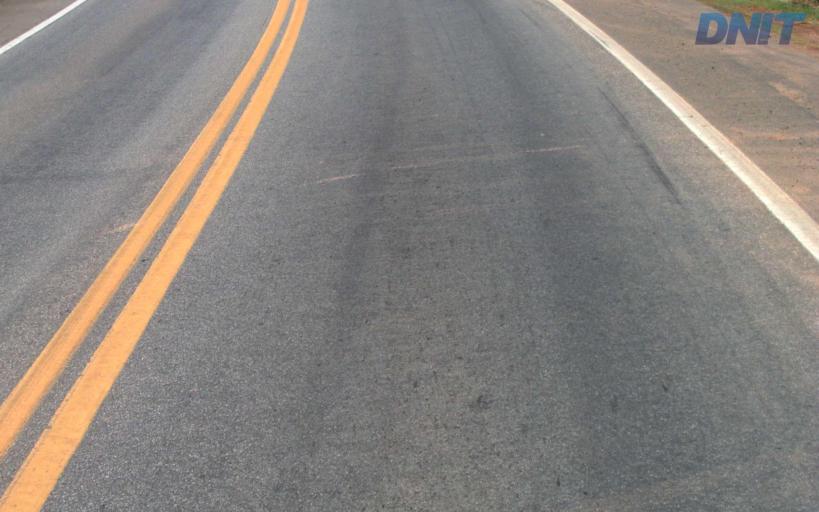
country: BR
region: Minas Gerais
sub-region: Ipatinga
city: Ipatinga
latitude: -19.4238
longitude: -42.4959
